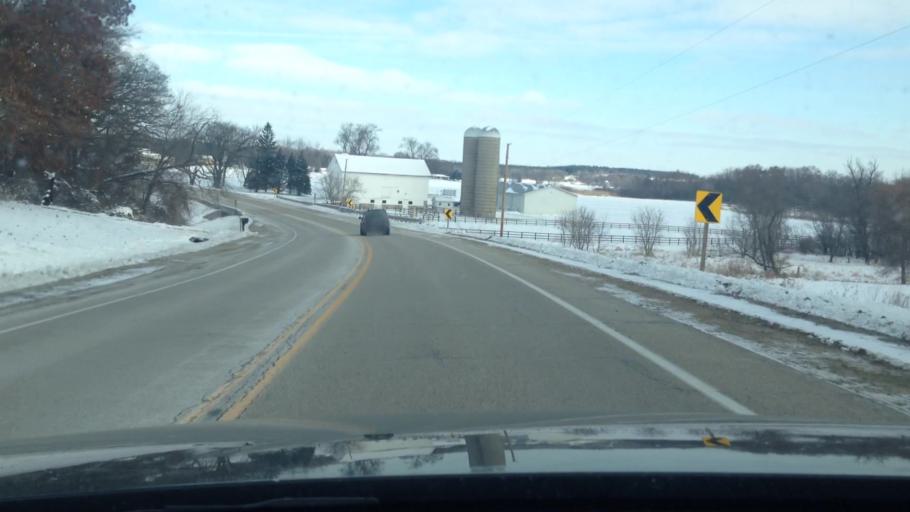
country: US
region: Wisconsin
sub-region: Walworth County
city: Lake Geneva
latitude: 42.6331
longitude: -88.4128
